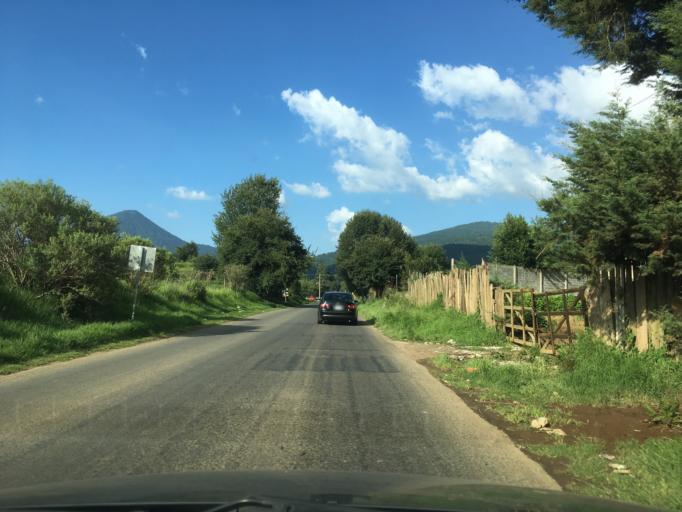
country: MX
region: Michoacan
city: Nahuatzen
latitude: 19.6463
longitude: -101.9203
